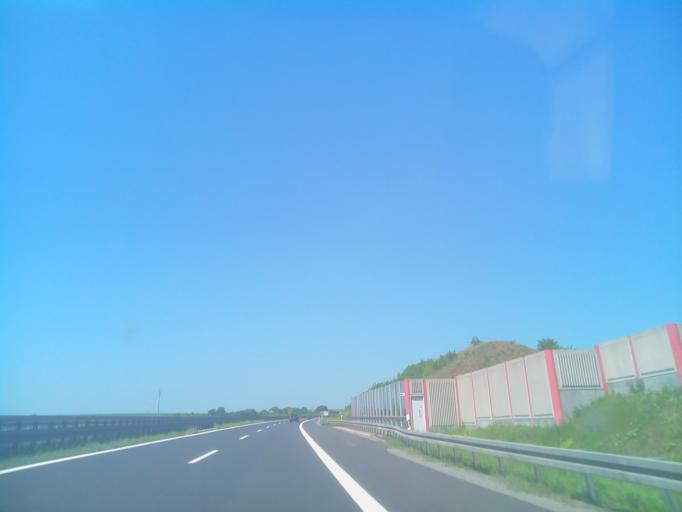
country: DE
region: Bavaria
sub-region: Regierungsbezirk Unterfranken
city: Oerlenbach
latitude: 50.1306
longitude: 10.1498
